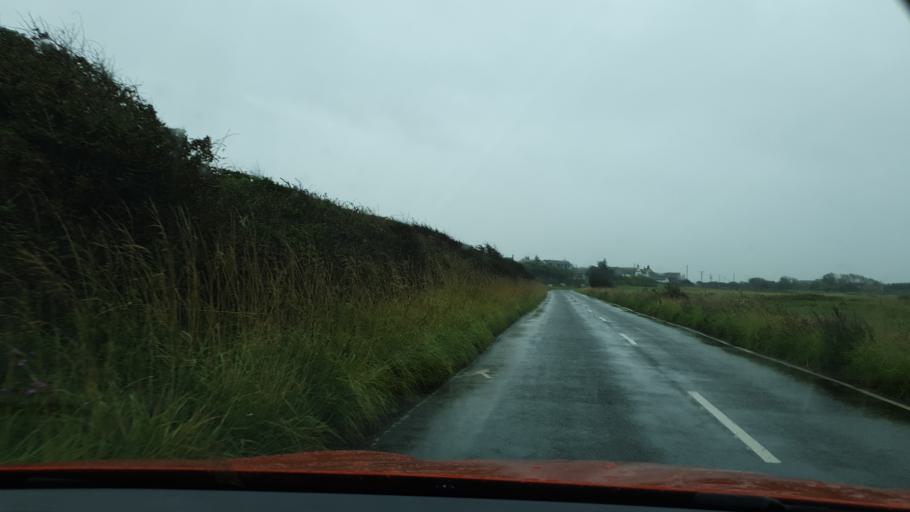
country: GB
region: England
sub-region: Cumbria
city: Barrow in Furness
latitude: 54.0870
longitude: -3.2403
